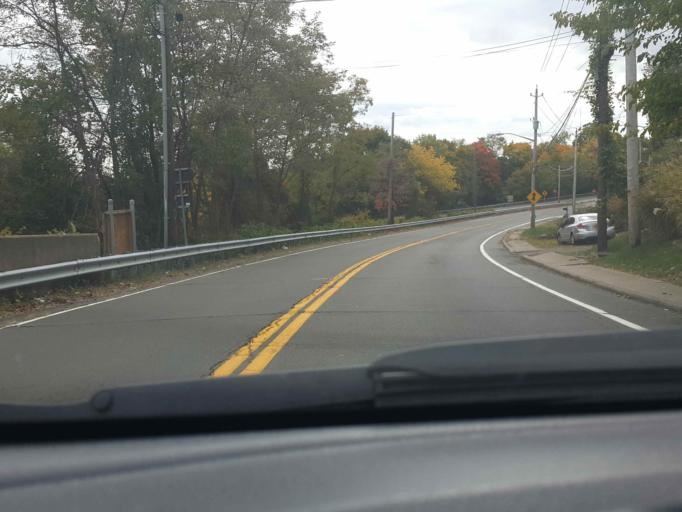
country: US
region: New York
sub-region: Rockland County
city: South Nyack
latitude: 41.0802
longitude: -73.9234
